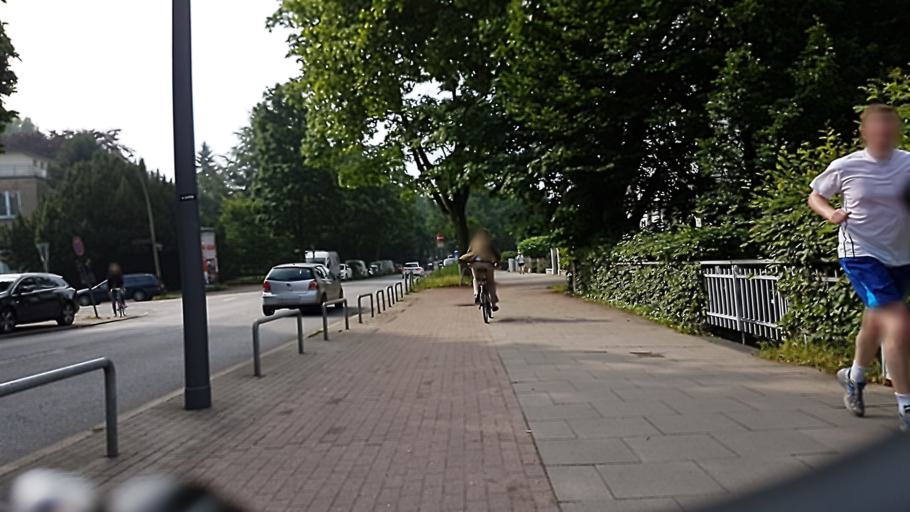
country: DE
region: Hamburg
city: Hamburg
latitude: 53.5771
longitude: 10.0102
